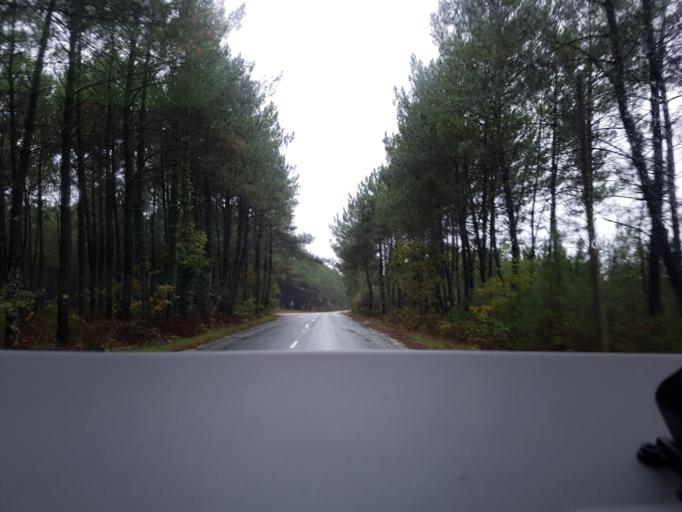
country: FR
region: Aquitaine
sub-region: Departement de la Gironde
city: Belin-Beliet
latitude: 44.5141
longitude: -0.7497
